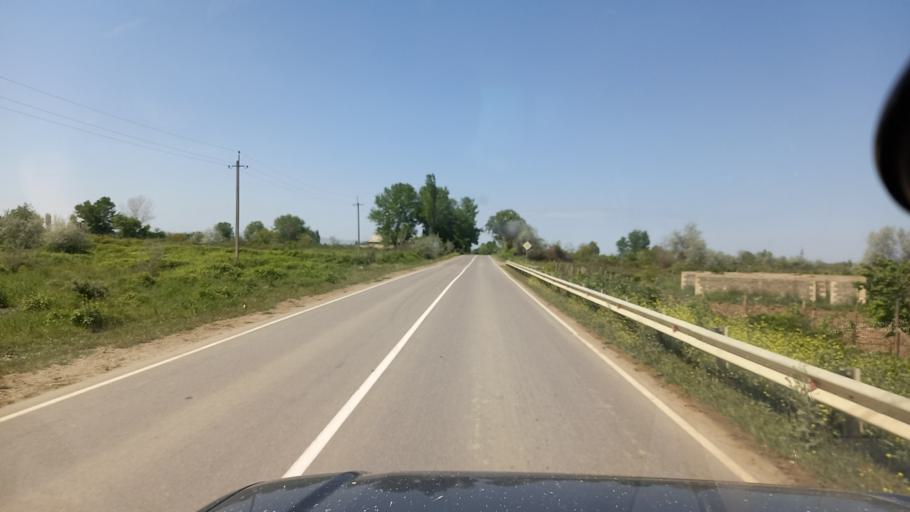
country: RU
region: Dagestan
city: Novaya Maka
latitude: 41.8119
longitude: 48.4049
